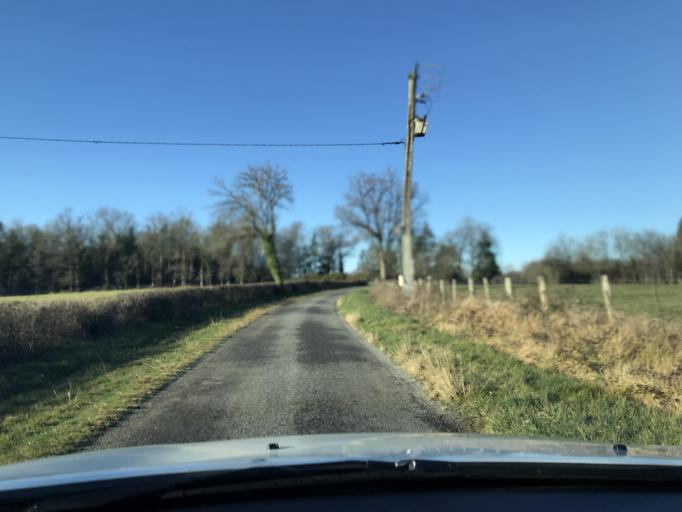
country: FR
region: Poitou-Charentes
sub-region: Departement de la Charente
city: Chasseneuil-sur-Bonnieure
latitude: 45.8390
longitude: 0.5235
